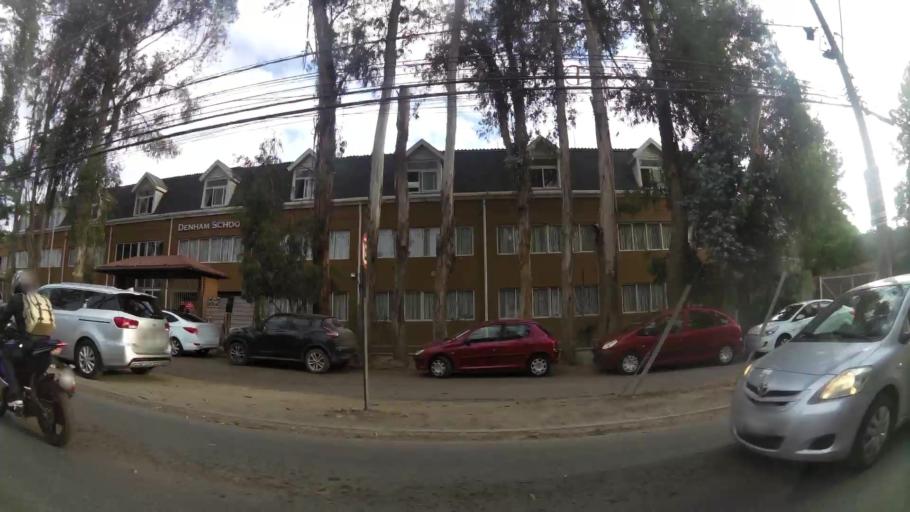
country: CL
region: Santiago Metropolitan
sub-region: Provincia de Maipo
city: San Bernardo
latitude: -33.6393
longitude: -70.6751
